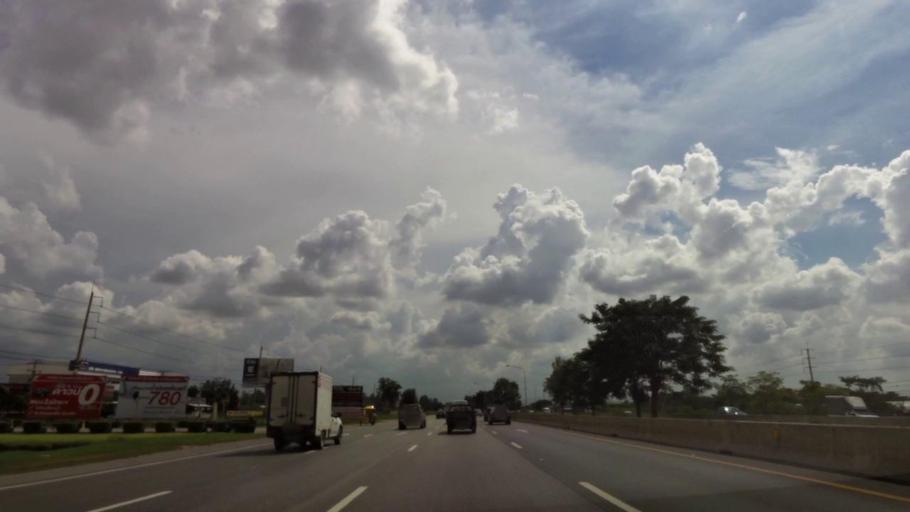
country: TH
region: Phra Nakhon Si Ayutthaya
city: Phra Nakhon Si Ayutthaya
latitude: 14.2948
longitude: 100.6134
